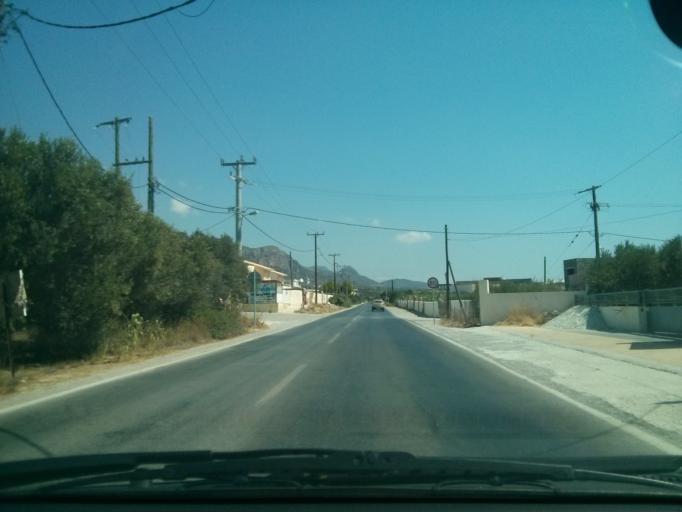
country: GR
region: Crete
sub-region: Nomos Lasithiou
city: Kato Chorio
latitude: 35.0024
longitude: 25.8001
